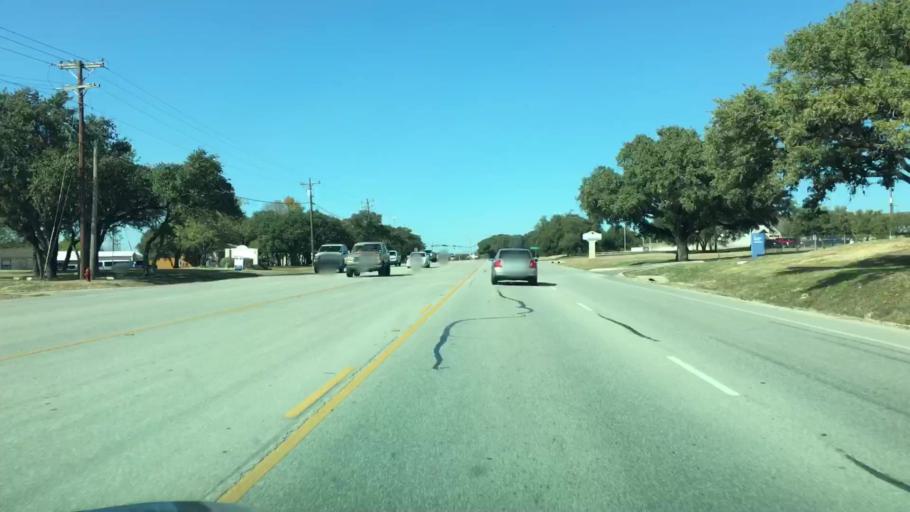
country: US
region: Texas
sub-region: Hays County
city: Dripping Springs
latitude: 30.1995
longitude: -98.1084
